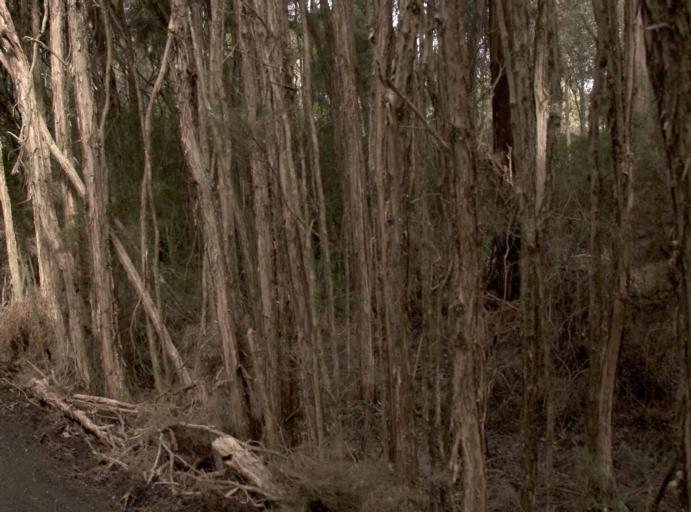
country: AU
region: Tasmania
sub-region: Launceston
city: Mayfield
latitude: -41.2764
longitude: 147.1882
